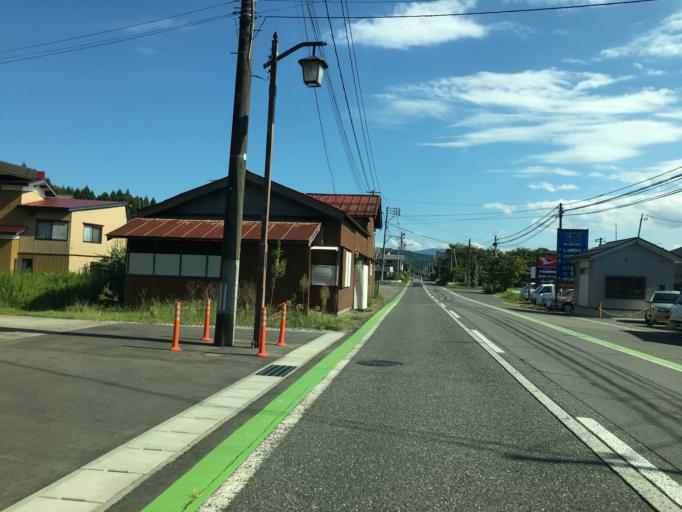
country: JP
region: Niigata
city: Suibara
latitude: 37.6743
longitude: 139.4646
